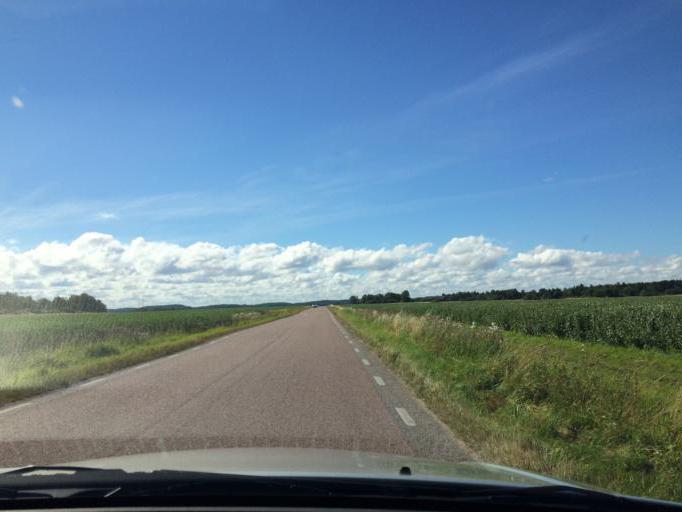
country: SE
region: Soedermanland
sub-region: Eskilstuna Kommun
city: Torshalla
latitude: 59.5428
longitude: 16.4481
